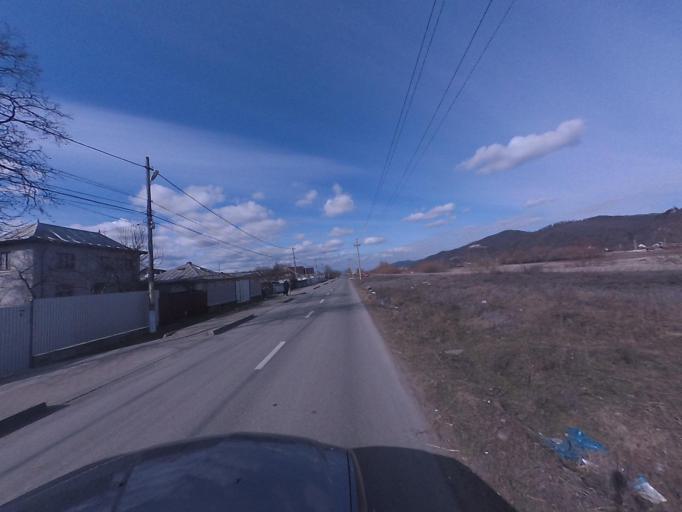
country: RO
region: Neamt
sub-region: Oras Targu Neamt
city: Humulesti
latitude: 47.2009
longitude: 26.3547
